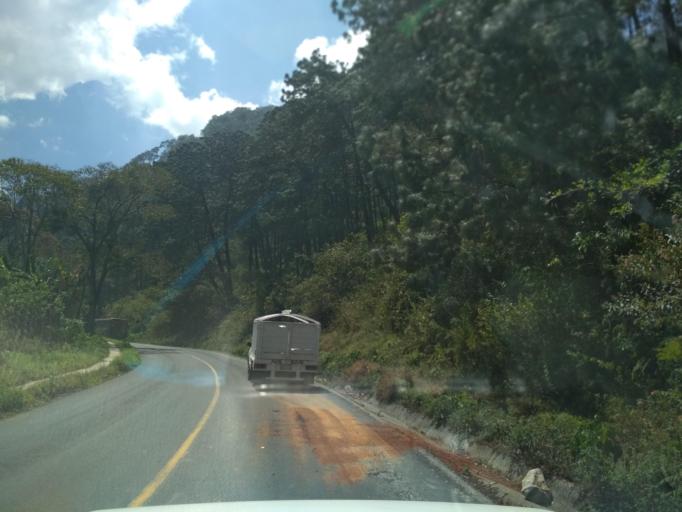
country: MX
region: Veracruz
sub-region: Tlilapan
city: Tonalixco
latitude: 18.7813
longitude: -97.0834
